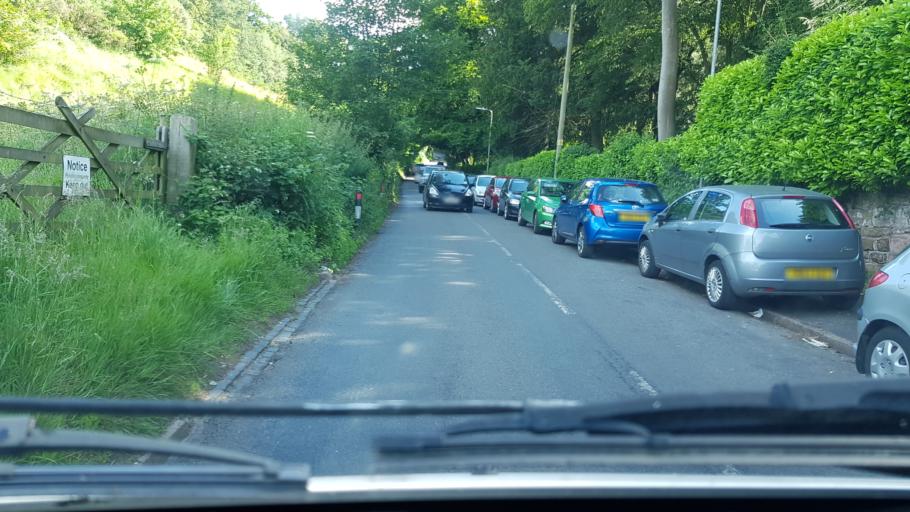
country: GB
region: England
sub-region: Worcestershire
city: Bewdley
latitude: 52.3717
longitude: -2.3124
